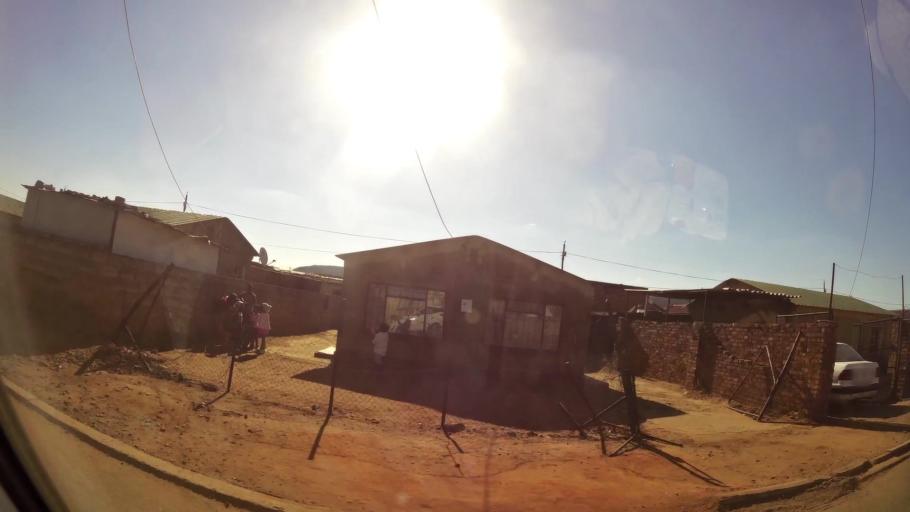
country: ZA
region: Gauteng
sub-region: City of Tshwane Metropolitan Municipality
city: Cullinan
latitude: -25.7130
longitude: 28.3817
